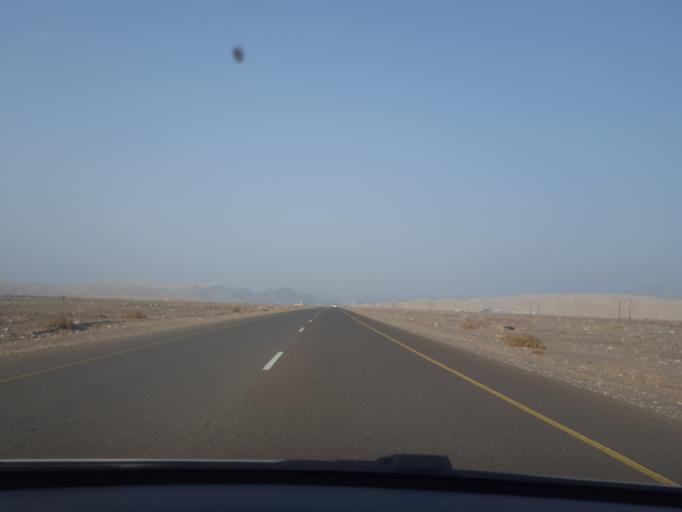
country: AE
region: Abu Dhabi
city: Al Ain
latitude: 24.0284
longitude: 55.9882
